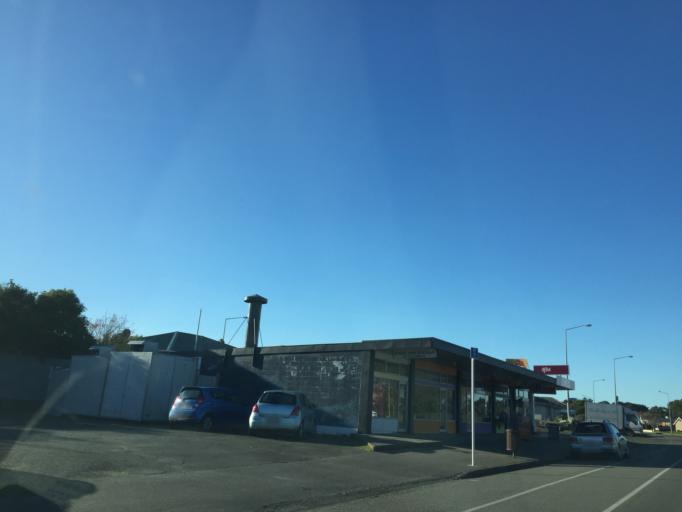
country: NZ
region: Southland
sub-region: Invercargill City
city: Invercargill
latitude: -46.4059
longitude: 168.3762
